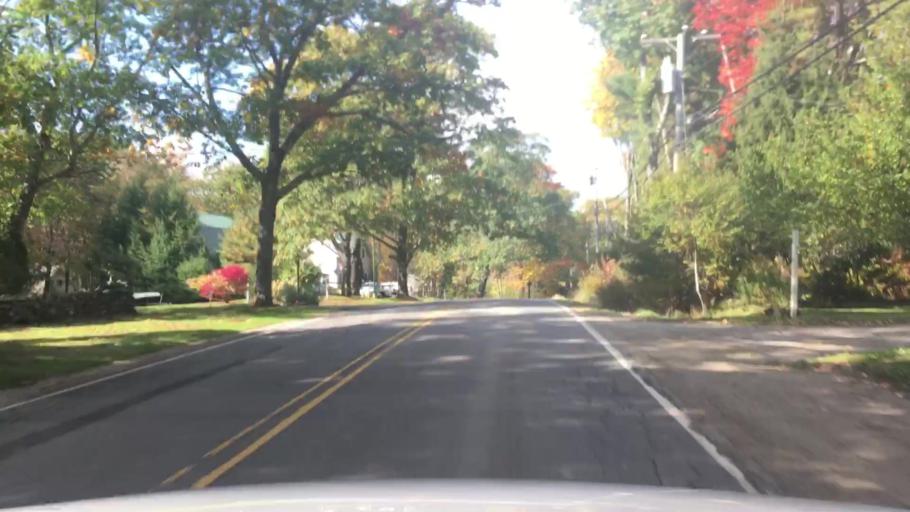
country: US
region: Maine
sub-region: Knox County
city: Warren
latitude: 44.1487
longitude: -69.2371
